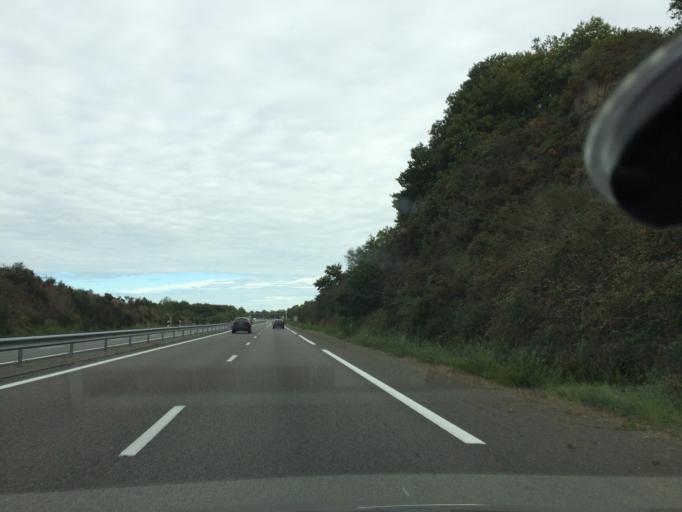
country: FR
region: Brittany
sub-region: Departement d'Ille-et-Vilaine
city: Saint-Pierre-de-Plesguen
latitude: 48.4540
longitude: -1.9205
